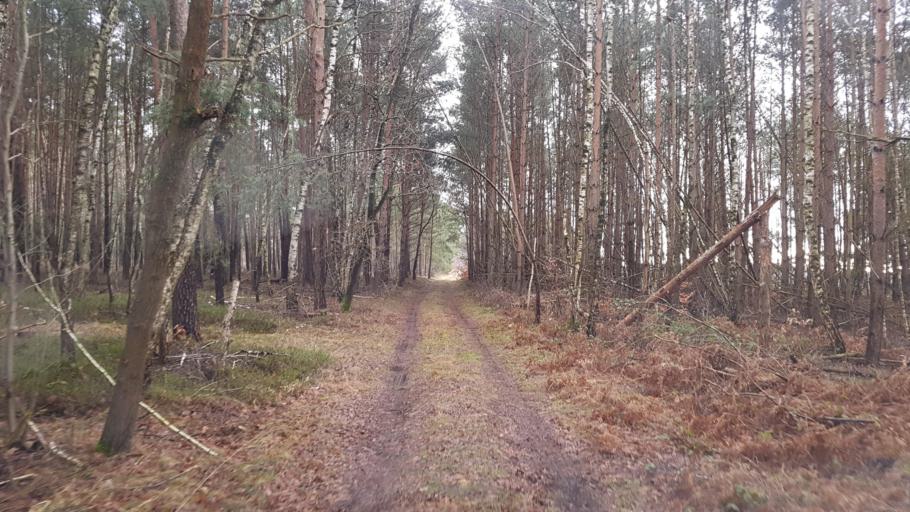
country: DE
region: Brandenburg
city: Ruckersdorf
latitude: 51.5584
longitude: 13.6181
